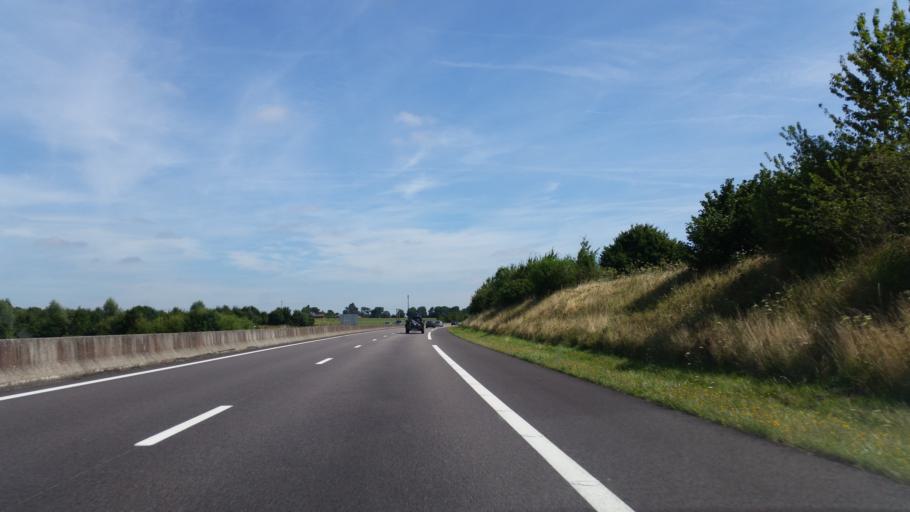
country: FR
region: Haute-Normandie
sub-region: Departement de la Seine-Maritime
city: Aumale
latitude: 49.7746
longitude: 1.7184
